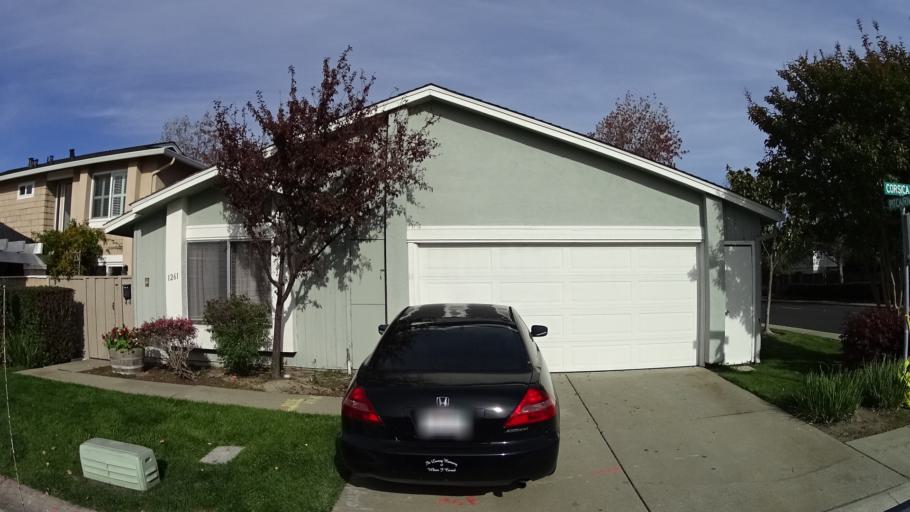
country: US
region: California
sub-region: San Mateo County
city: Redwood Shores
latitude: 37.5398
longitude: -122.2658
